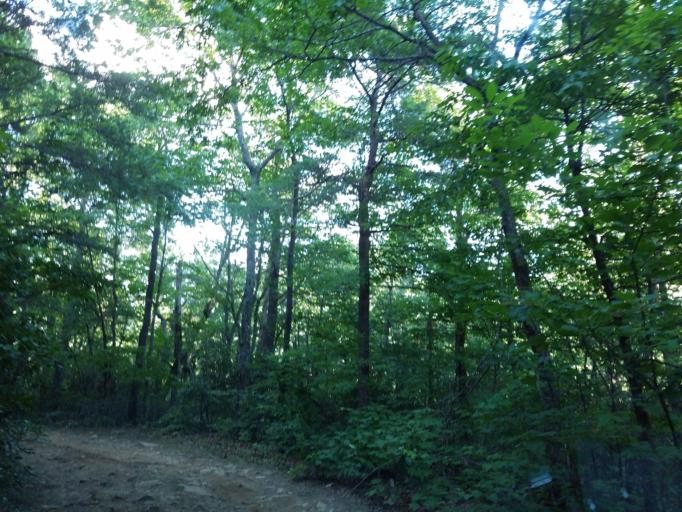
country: US
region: Georgia
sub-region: Dawson County
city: Dawsonville
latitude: 34.6192
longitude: -84.2268
